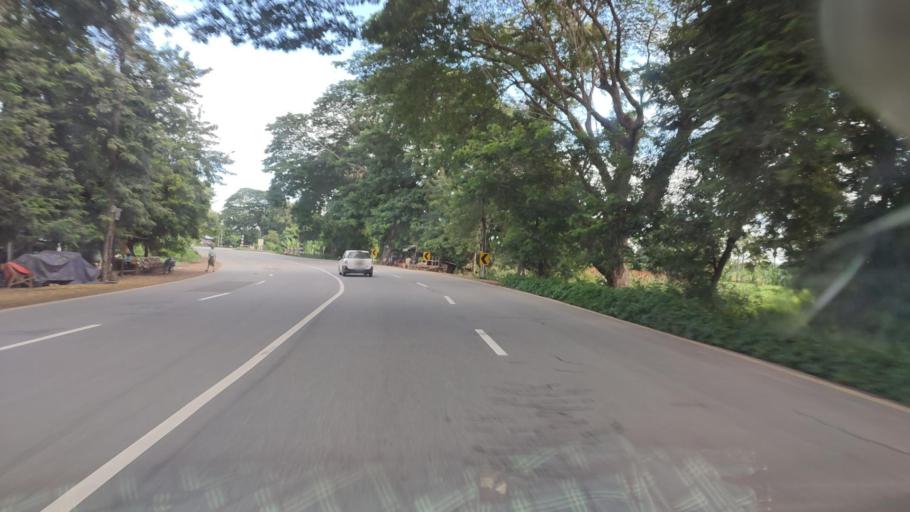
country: MM
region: Mandalay
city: Yamethin
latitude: 20.2206
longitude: 96.1806
